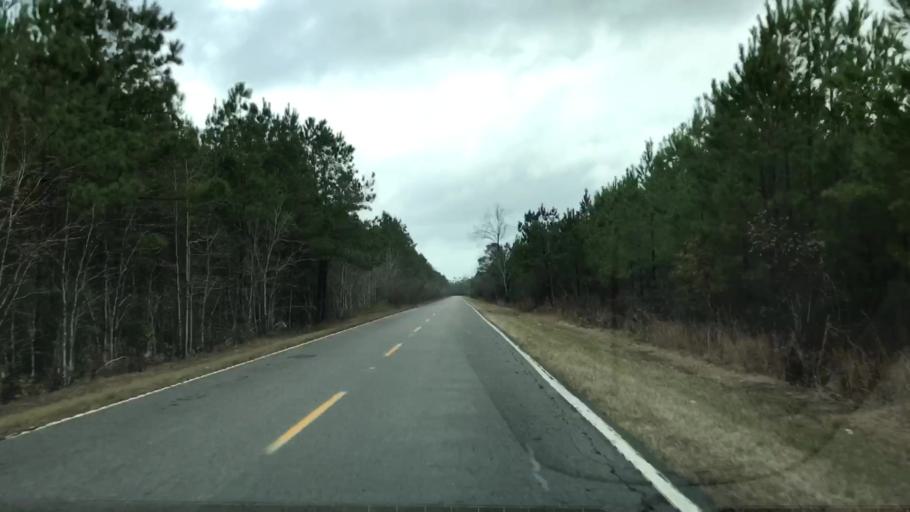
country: US
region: South Carolina
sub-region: Georgetown County
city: Murrells Inlet
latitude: 33.6270
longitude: -79.2425
